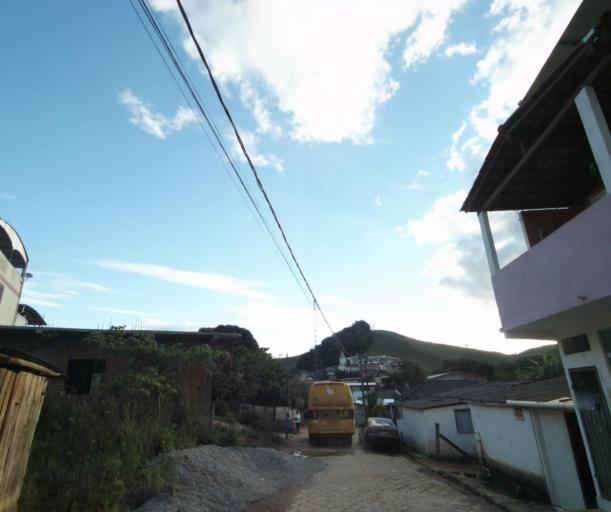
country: BR
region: Espirito Santo
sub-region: Guacui
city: Guacui
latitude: -20.6181
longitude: -41.6820
